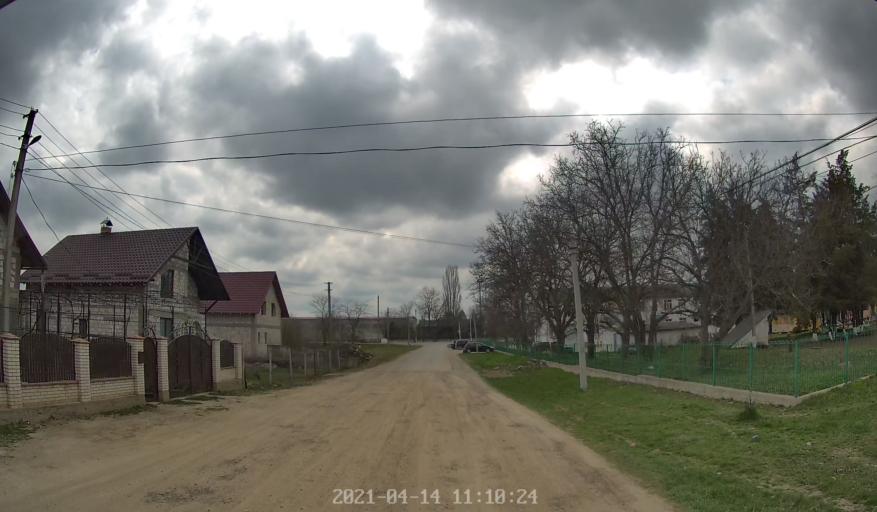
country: MD
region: Criuleni
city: Criuleni
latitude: 47.1560
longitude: 29.1479
